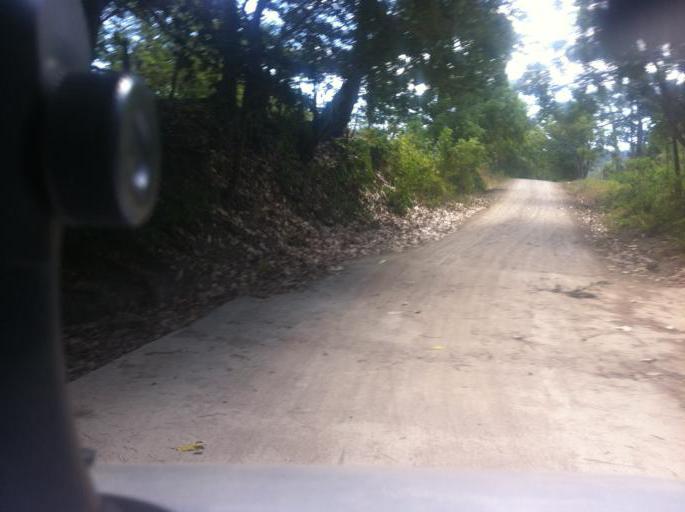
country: NI
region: Rivas
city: Belen
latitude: 11.5876
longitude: -86.0249
